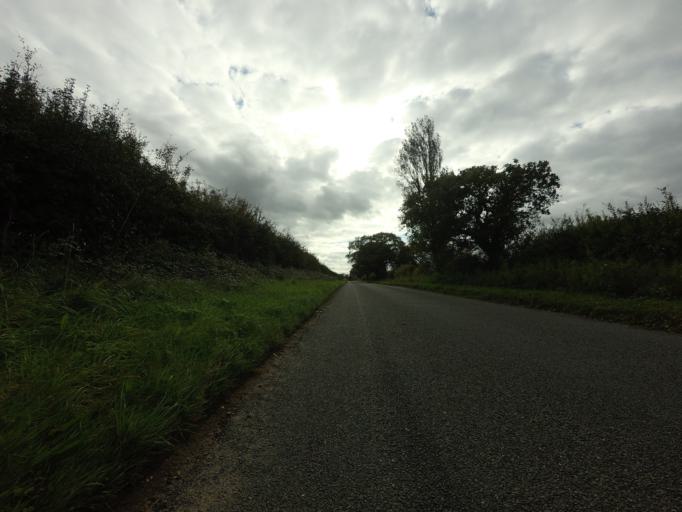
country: GB
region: England
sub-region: Norfolk
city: Snettisham
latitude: 52.8904
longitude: 0.5276
